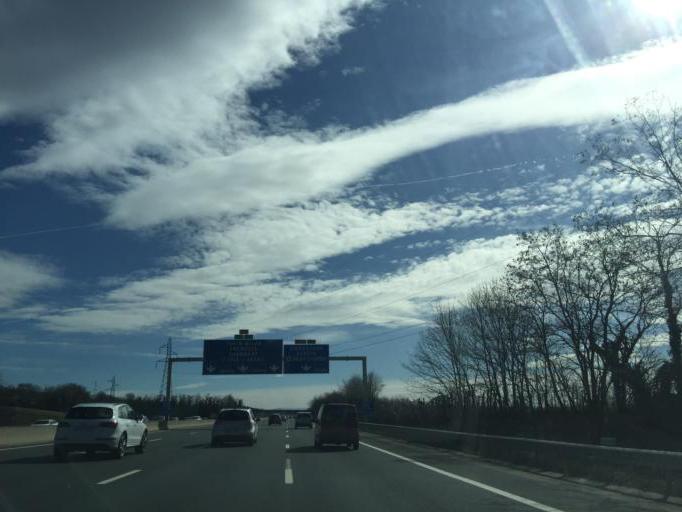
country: FR
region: Rhone-Alpes
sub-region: Departement du Rhone
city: Saint-Laurent-de-Mure
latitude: 45.6767
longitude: 5.0309
